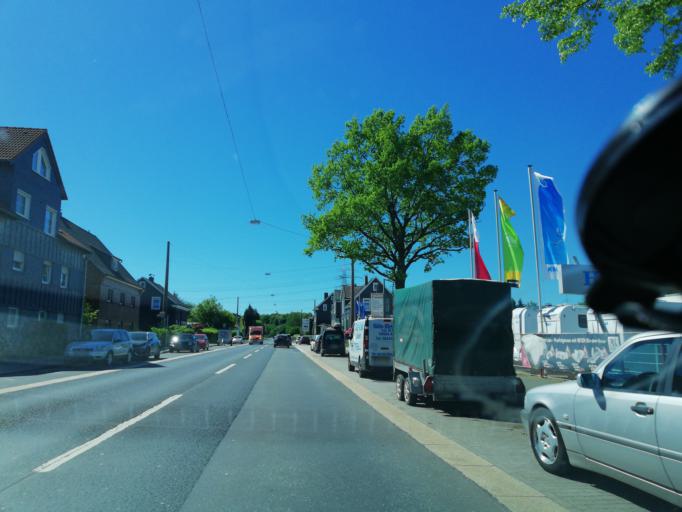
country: DE
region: North Rhine-Westphalia
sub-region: Regierungsbezirk Dusseldorf
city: Remscheid
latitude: 51.2318
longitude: 7.2356
